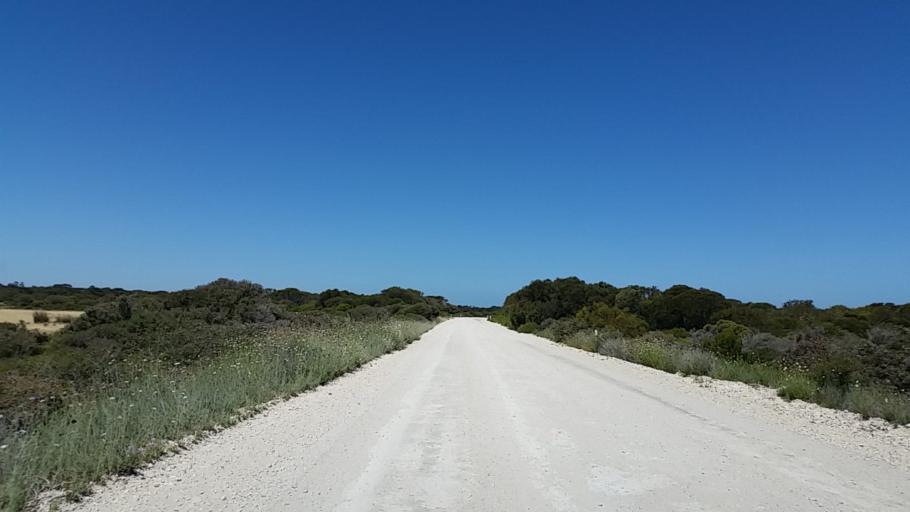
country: AU
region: South Australia
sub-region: Yorke Peninsula
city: Honiton
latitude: -35.2136
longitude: 137.0348
